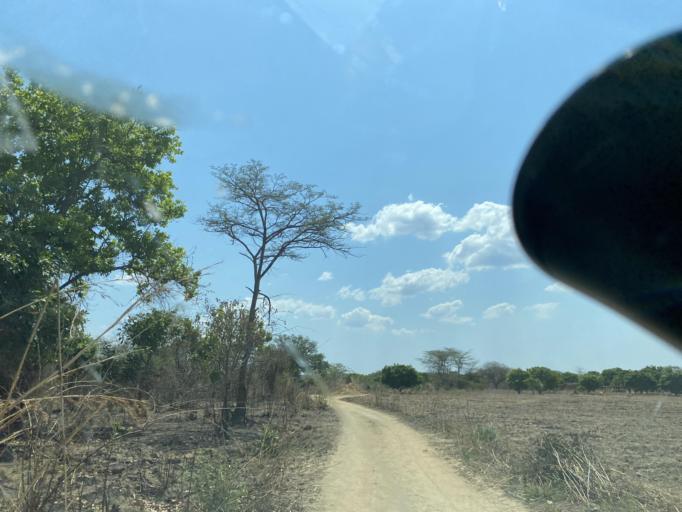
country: ZM
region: Lusaka
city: Chongwe
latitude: -15.0811
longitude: 29.5098
